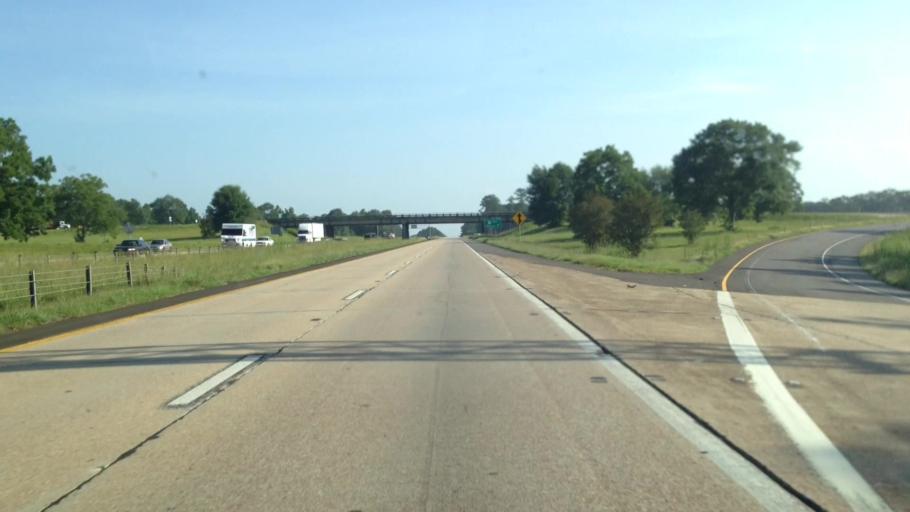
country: US
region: Mississippi
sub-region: Pike County
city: Summit
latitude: 31.2860
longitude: -90.4786
